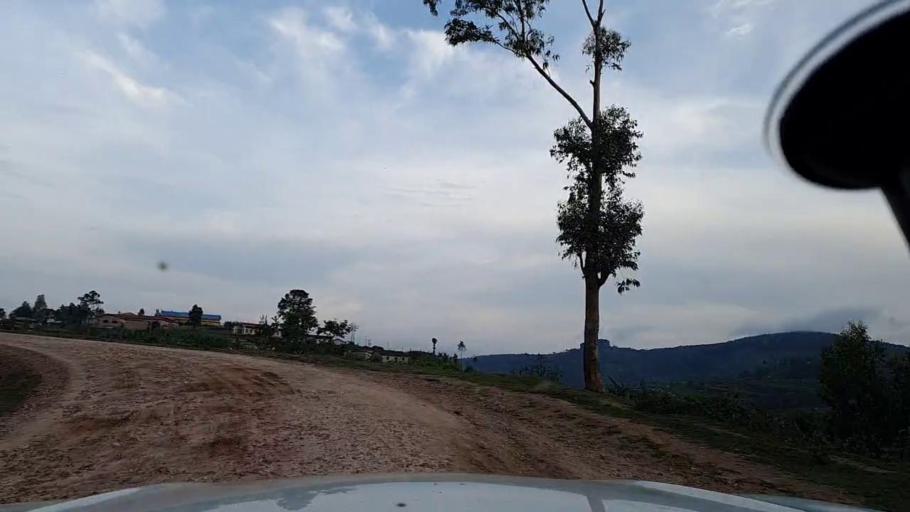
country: RW
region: Southern Province
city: Nyanza
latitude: -2.2213
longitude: 29.6460
